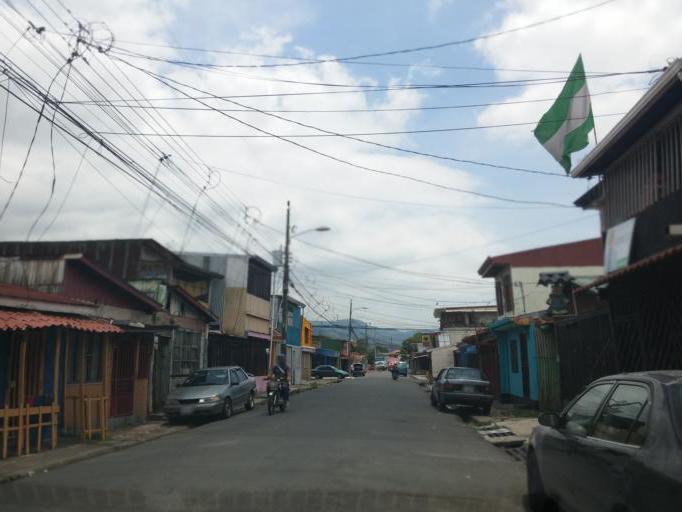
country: CR
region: San Jose
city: Alajuelita
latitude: 9.9057
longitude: -84.0828
